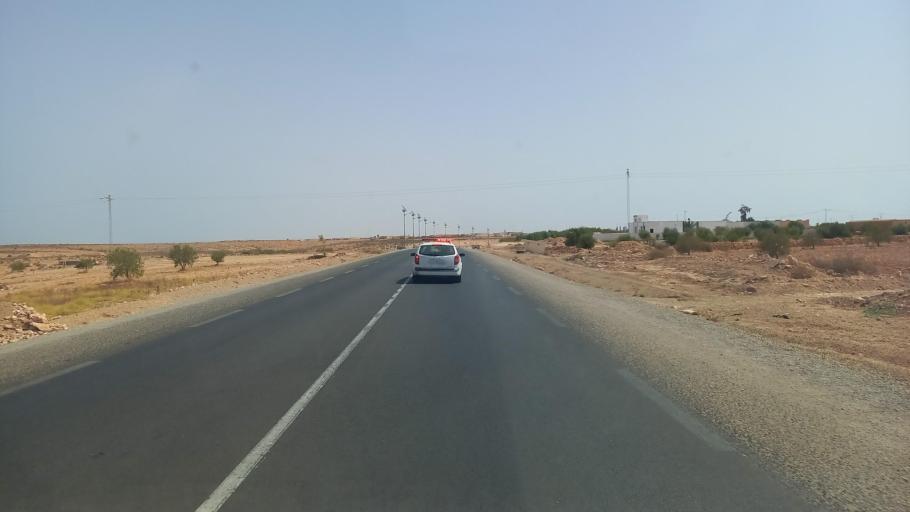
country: TN
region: Madanin
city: Medenine
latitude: 33.3691
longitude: 10.6738
